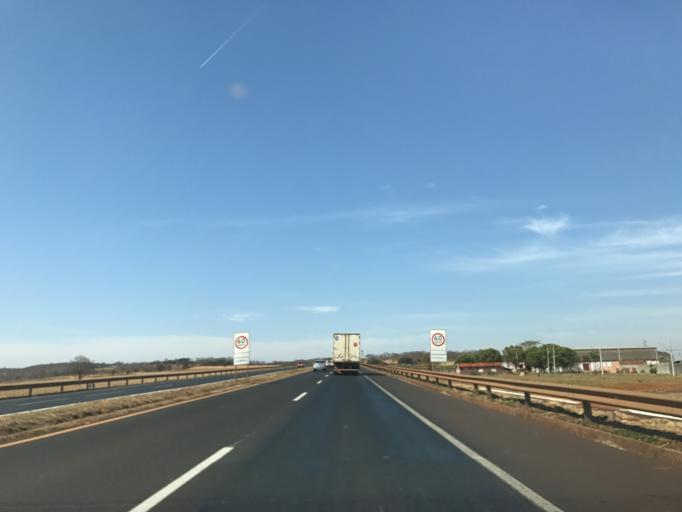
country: BR
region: Minas Gerais
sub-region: Centralina
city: Centralina
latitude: -18.5979
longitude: -49.1924
